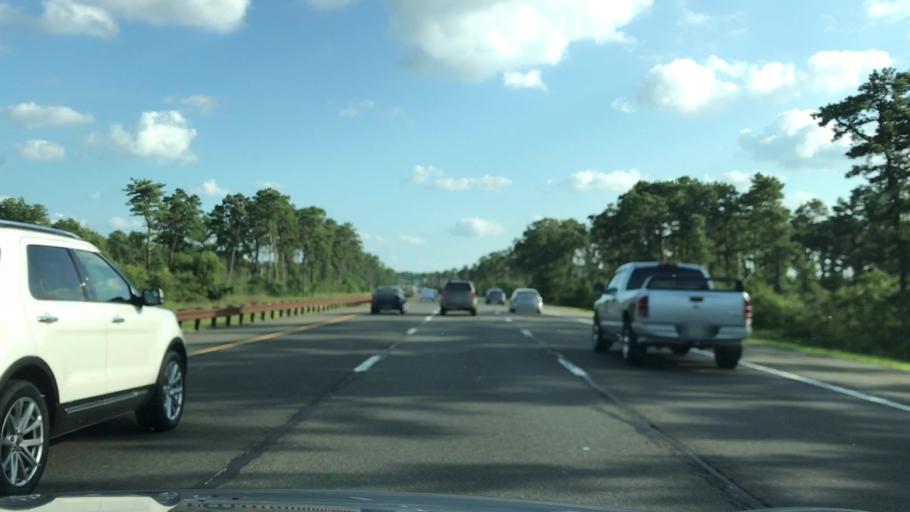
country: US
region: New Jersey
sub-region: Ocean County
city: South Toms River
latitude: 39.9150
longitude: -74.2118
